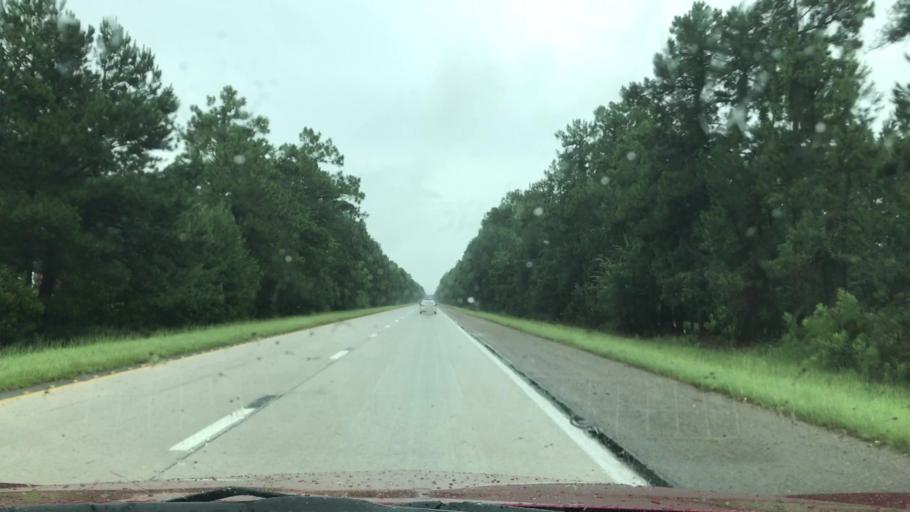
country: US
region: South Carolina
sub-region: Orangeburg County
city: Holly Hill
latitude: 33.2047
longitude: -80.4052
